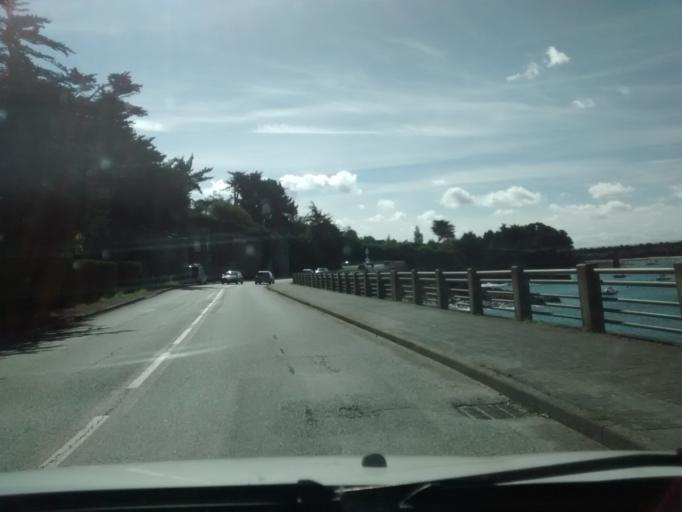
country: FR
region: Brittany
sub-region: Departement d'Ille-et-Vilaine
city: Saint-Briac-sur-Mer
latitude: 48.6200
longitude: -2.1378
